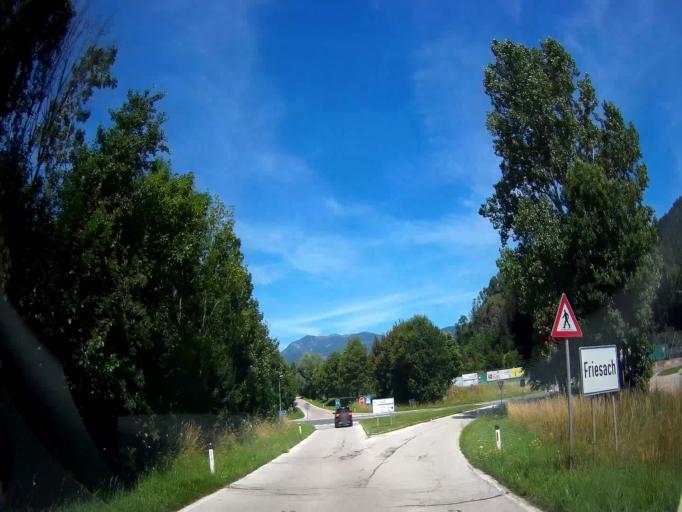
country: AT
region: Carinthia
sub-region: Politischer Bezirk Sankt Veit an der Glan
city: Friesach
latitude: 46.9520
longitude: 14.4193
